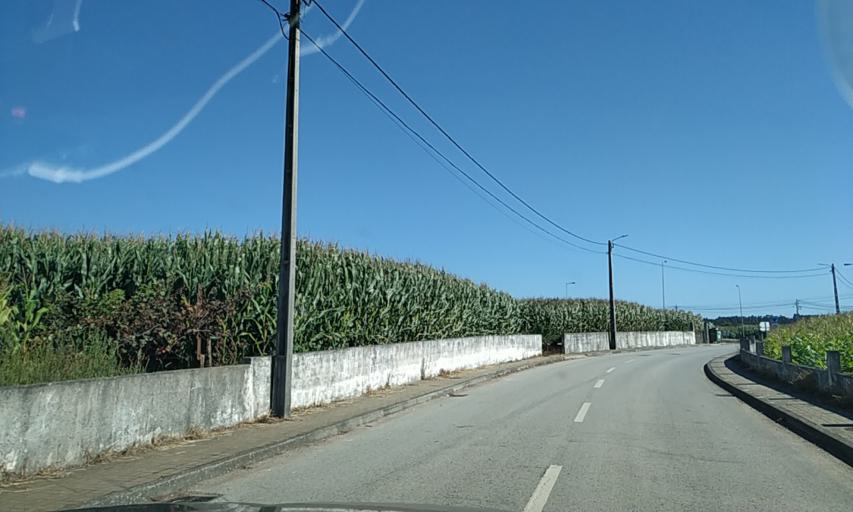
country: PT
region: Aveiro
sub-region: Estarreja
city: Salreu
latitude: 40.7438
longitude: -8.5462
